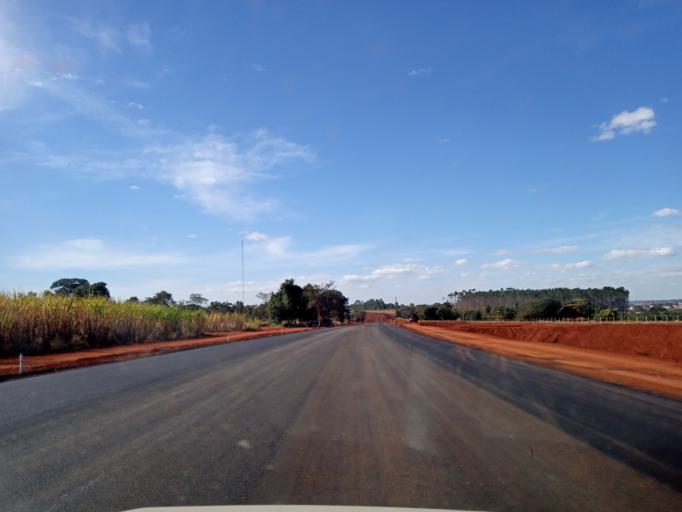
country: BR
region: Minas Gerais
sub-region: Ituiutaba
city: Ituiutaba
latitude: -18.9823
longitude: -49.5100
